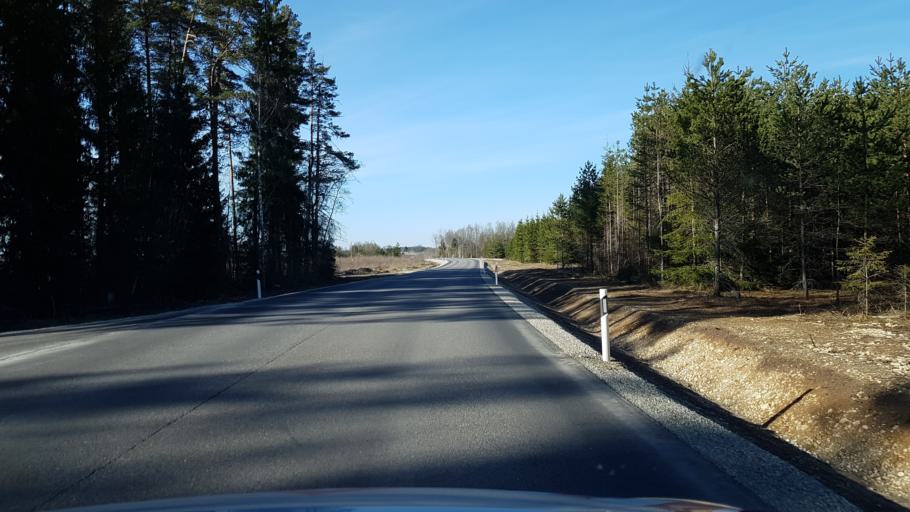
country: EE
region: Laeaene-Virumaa
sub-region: Vinni vald
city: Vinni
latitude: 59.1379
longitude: 26.5978
